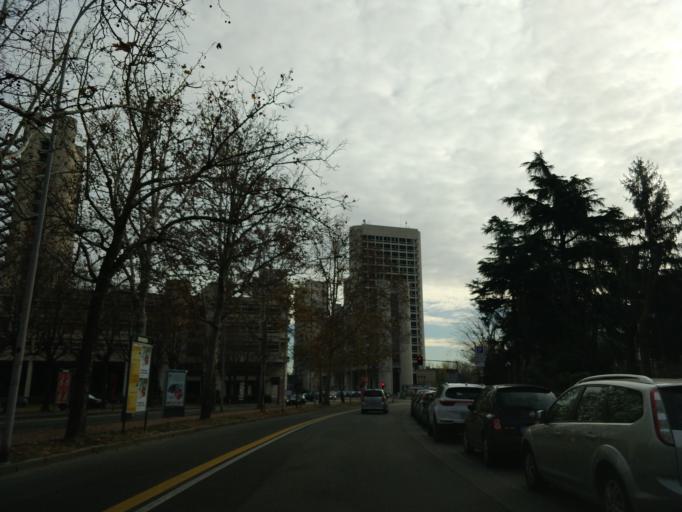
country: IT
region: Emilia-Romagna
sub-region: Provincia di Bologna
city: Bologna
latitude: 44.5099
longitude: 11.3613
